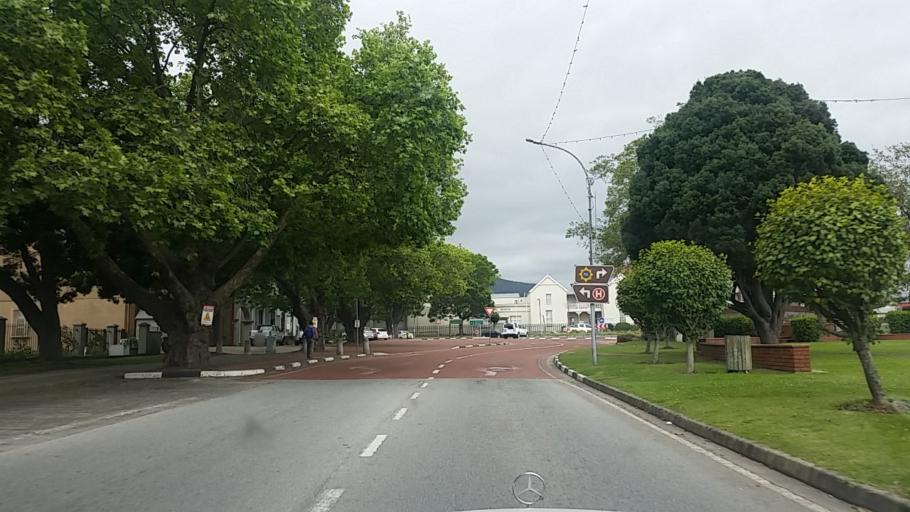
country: ZA
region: Western Cape
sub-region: Eden District Municipality
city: George
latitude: -33.9561
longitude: 22.4586
